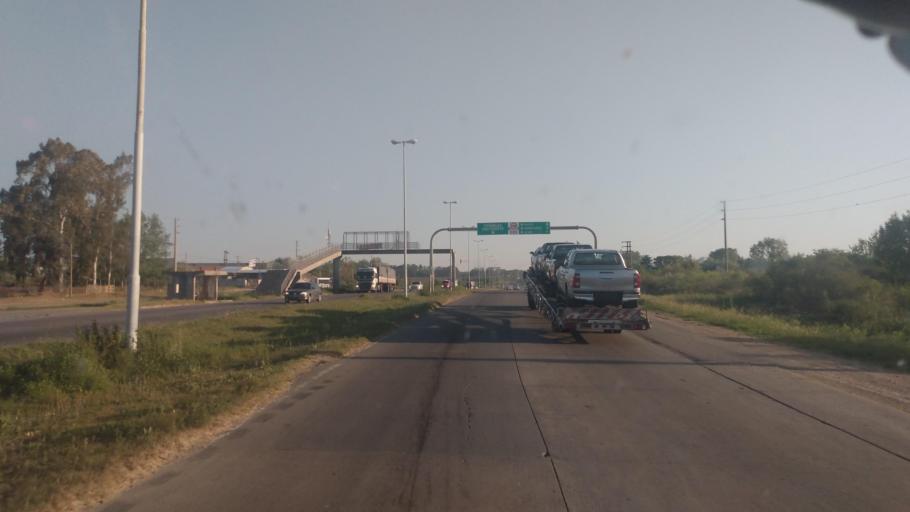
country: AR
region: Buenos Aires
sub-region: Partido de Campana
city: Campana
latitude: -34.2053
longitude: -58.9587
